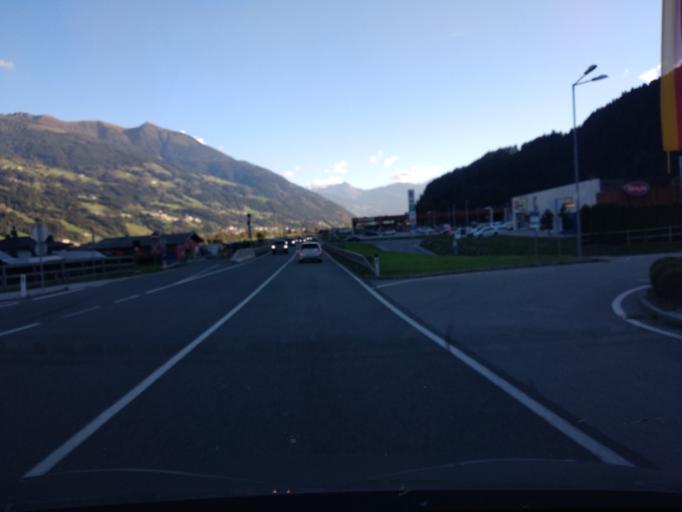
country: AT
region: Tyrol
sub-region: Politischer Bezirk Schwaz
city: Schlitters
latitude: 47.3764
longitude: 11.8436
